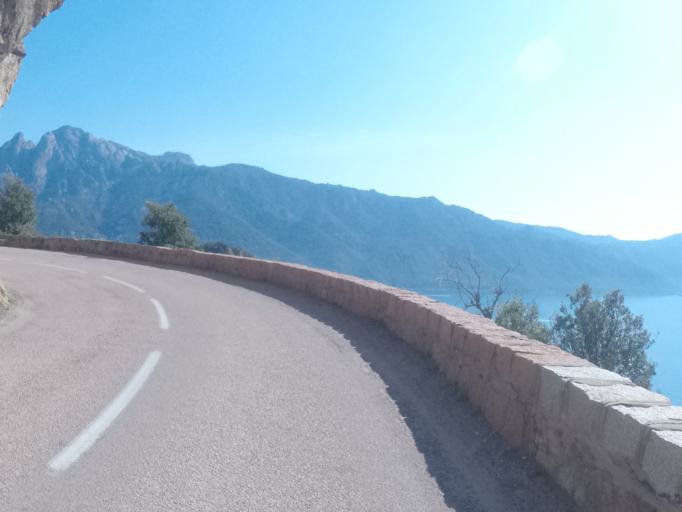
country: FR
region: Corsica
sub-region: Departement de la Corse-du-Sud
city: Cargese
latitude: 42.2911
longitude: 8.6790
